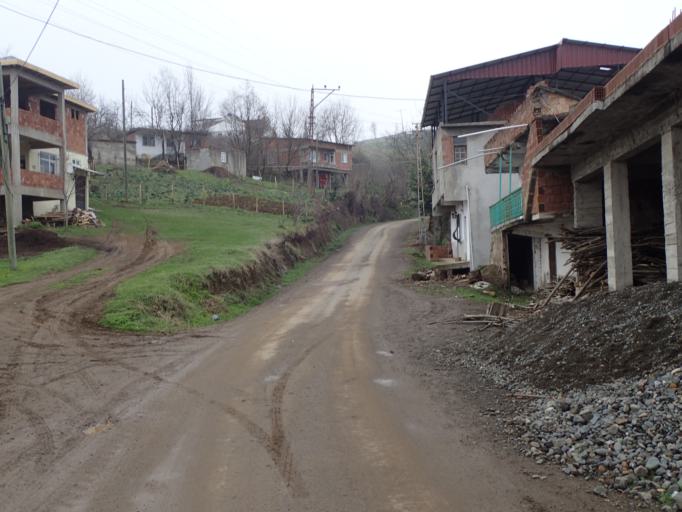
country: TR
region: Ordu
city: Camas
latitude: 40.9217
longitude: 37.5579
